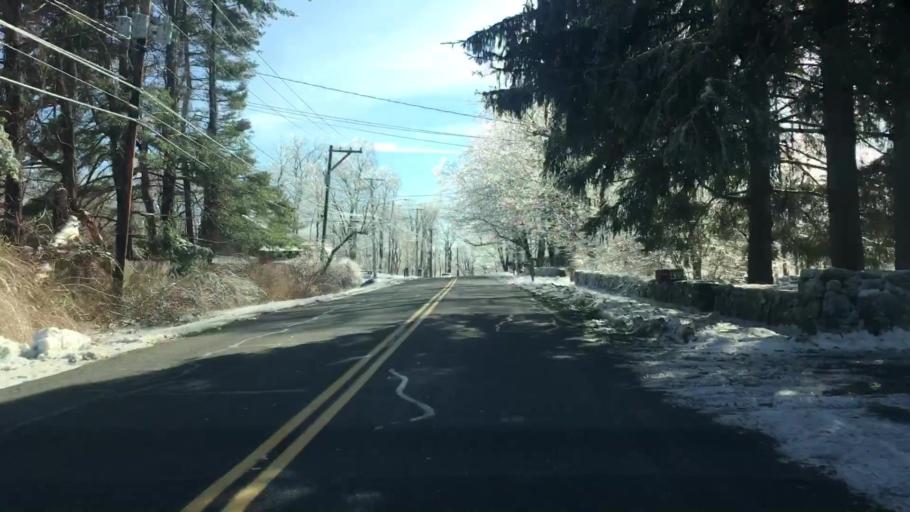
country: US
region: Connecticut
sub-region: Fairfield County
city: Trumbull
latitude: 41.3247
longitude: -73.2211
